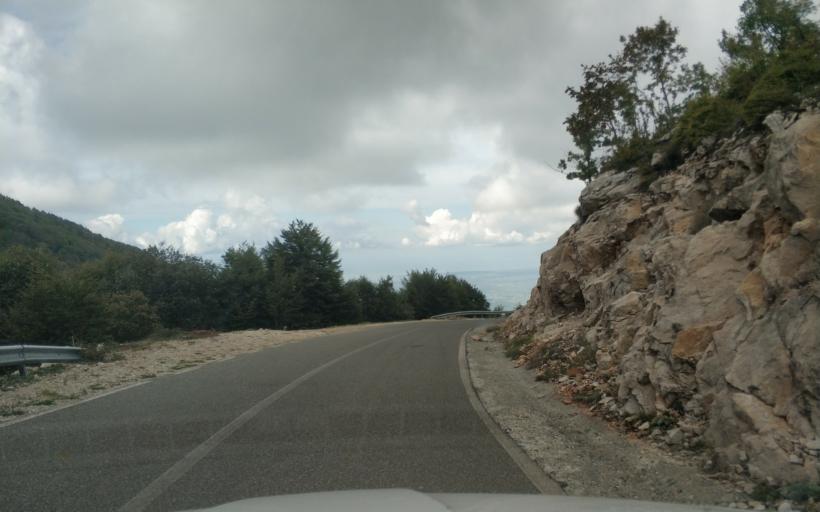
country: AL
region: Durres
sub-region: Rrethi i Krujes
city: Kruje
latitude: 41.5205
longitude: 19.8057
